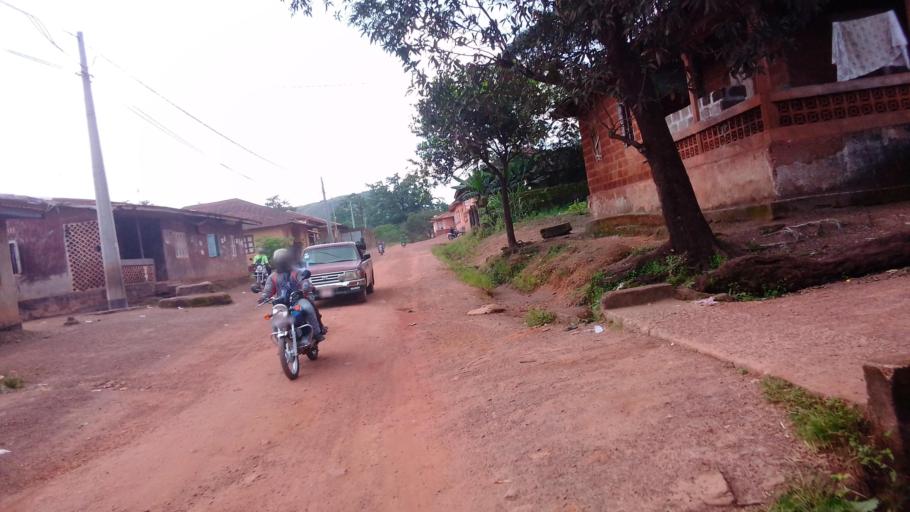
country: SL
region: Northern Province
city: Makeni
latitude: 8.8898
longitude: -12.0379
